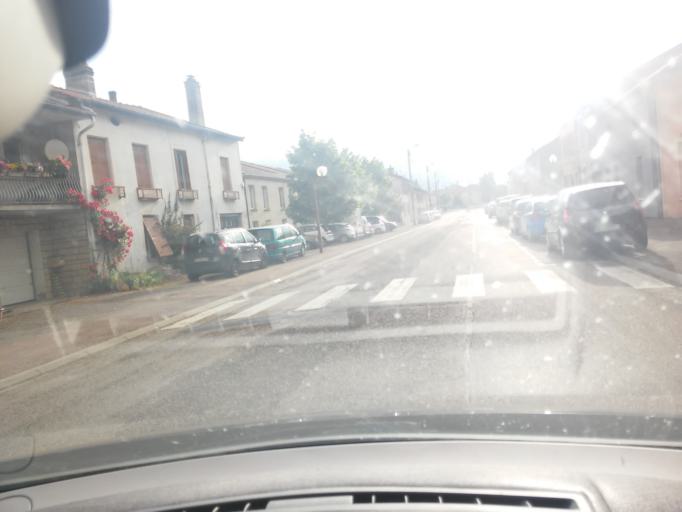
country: FR
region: Lorraine
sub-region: Departement de Meurthe-et-Moselle
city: Jarny
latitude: 49.0987
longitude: 5.8877
